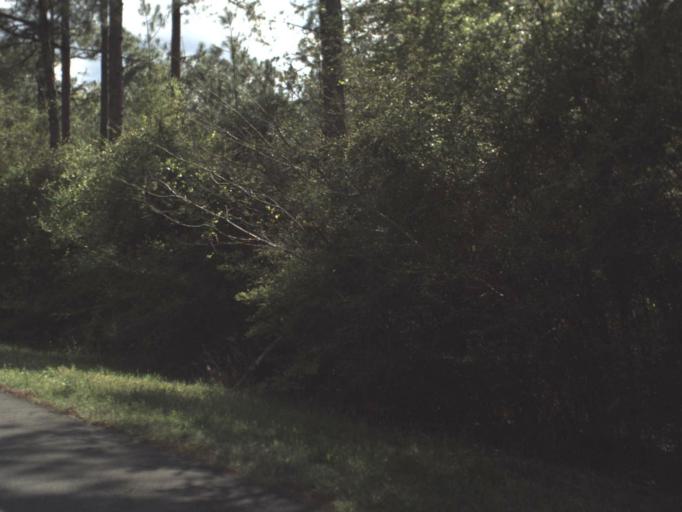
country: US
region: Florida
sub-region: Okaloosa County
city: Crestview
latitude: 30.8909
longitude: -86.5070
